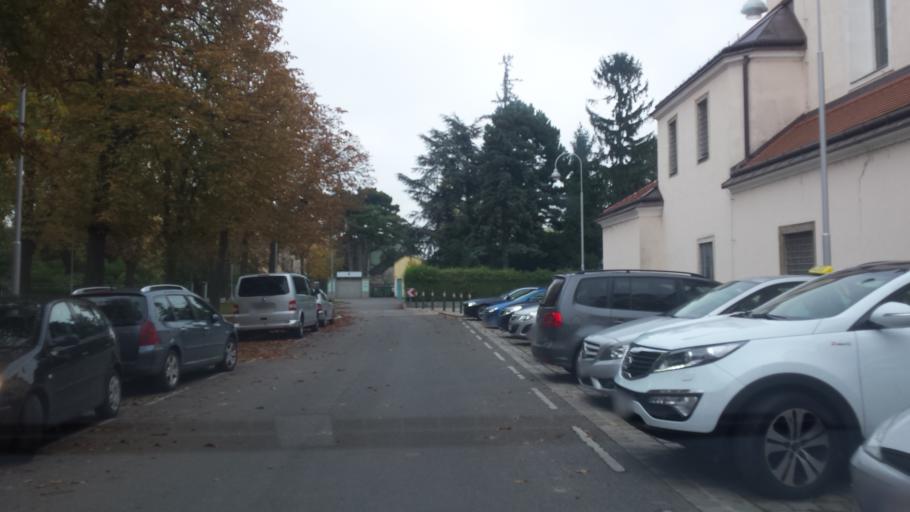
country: AT
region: Lower Austria
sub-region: Politischer Bezirk Wien-Umgebung
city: Schwechat
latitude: 48.1586
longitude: 16.4743
